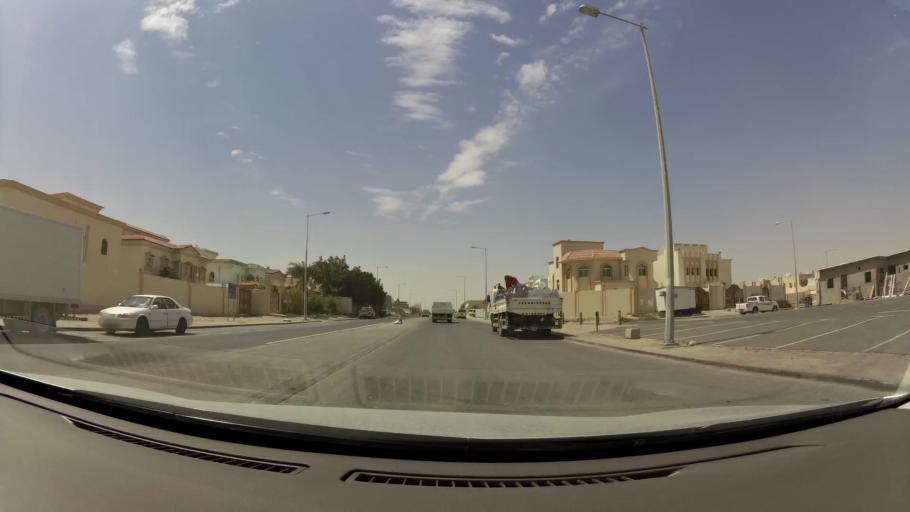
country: QA
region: Baladiyat ar Rayyan
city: Ar Rayyan
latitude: 25.2997
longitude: 51.4190
